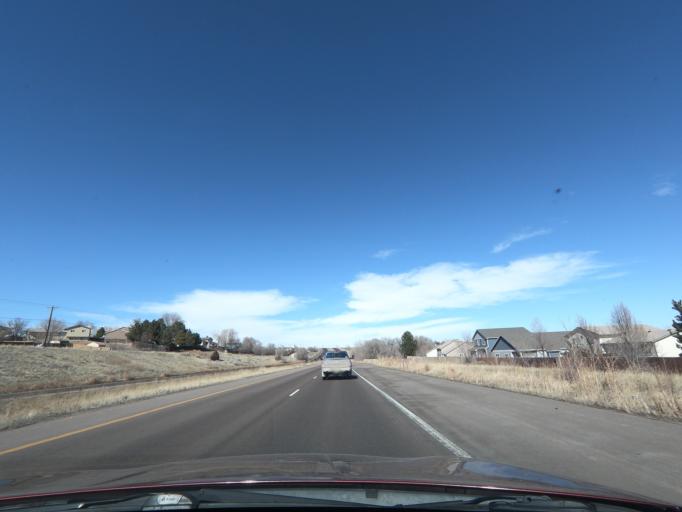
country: US
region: Colorado
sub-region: El Paso County
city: Security-Widefield
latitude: 38.7284
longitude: -104.6826
